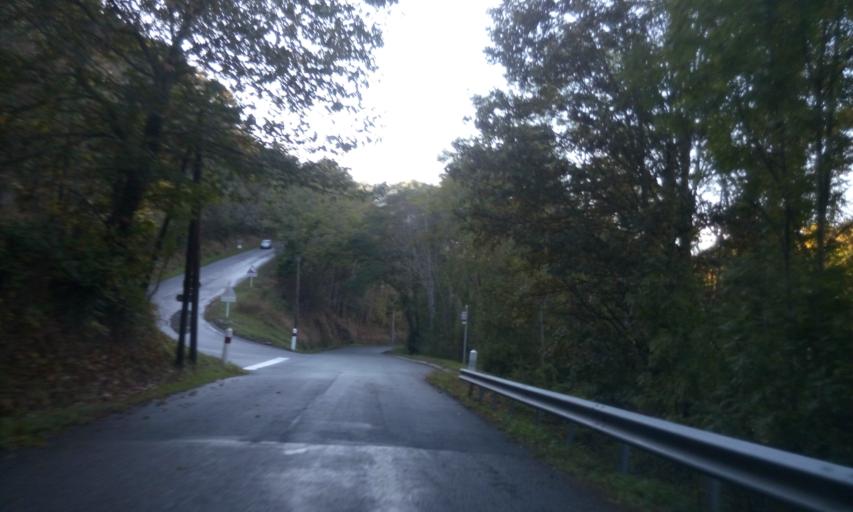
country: FR
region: Rhone-Alpes
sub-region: Departement du Rhone
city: Tarare
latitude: 45.9233
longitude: 4.4524
